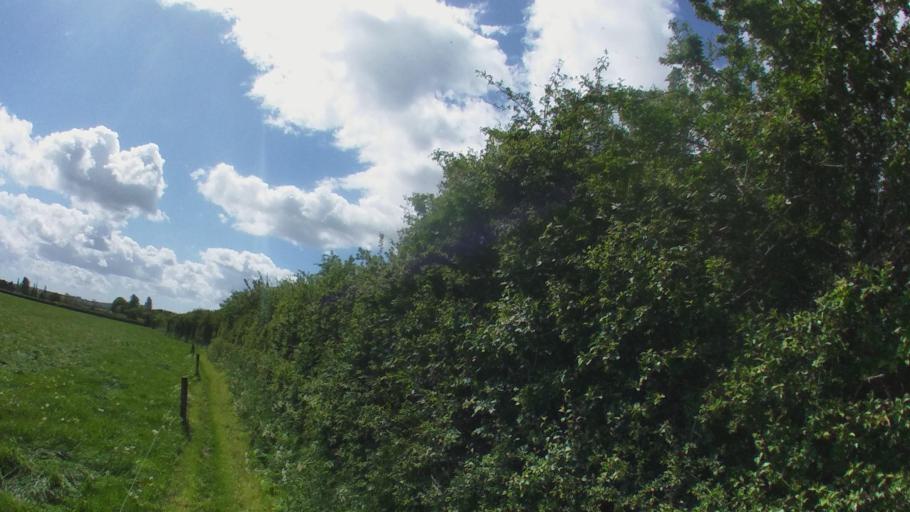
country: IE
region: Leinster
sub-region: Kilkenny
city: Thomastown
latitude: 52.5997
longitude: -7.1652
